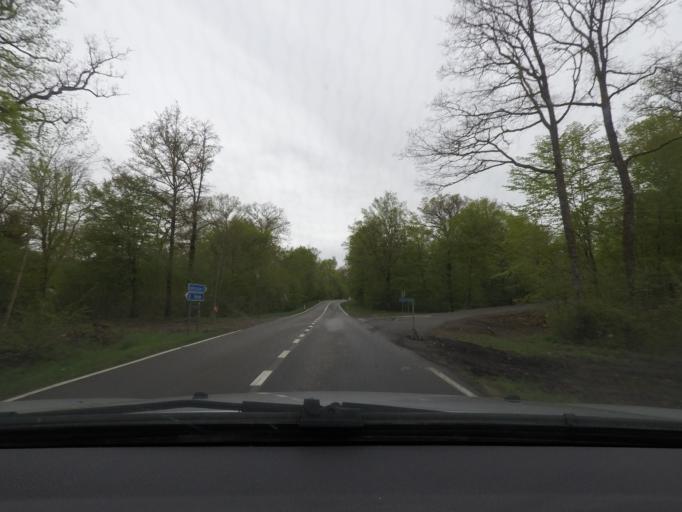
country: BE
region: Wallonia
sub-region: Province du Luxembourg
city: Tintigny
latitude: 49.6303
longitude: 5.5410
